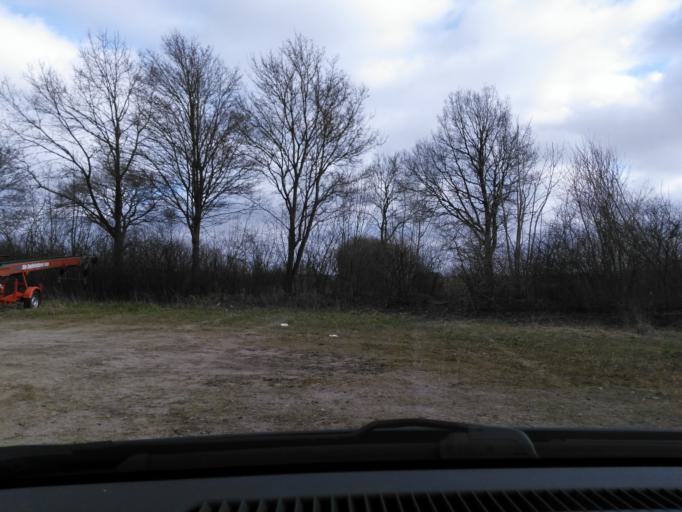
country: DE
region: Schleswig-Holstein
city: Molfsee
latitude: 54.2735
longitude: 10.0767
